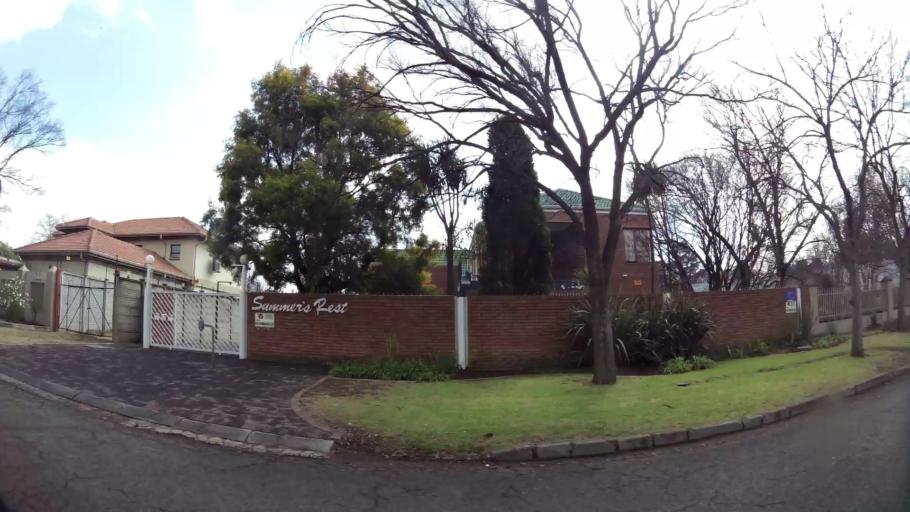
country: ZA
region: Gauteng
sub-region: Sedibeng District Municipality
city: Vanderbijlpark
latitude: -26.7418
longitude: 27.8340
